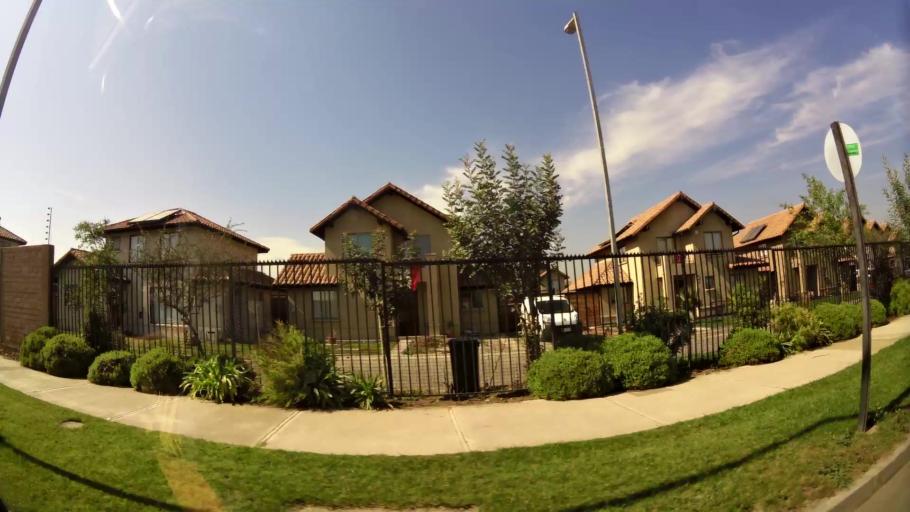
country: CL
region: Santiago Metropolitan
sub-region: Provincia de Talagante
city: Penaflor
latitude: -33.5629
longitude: -70.8297
